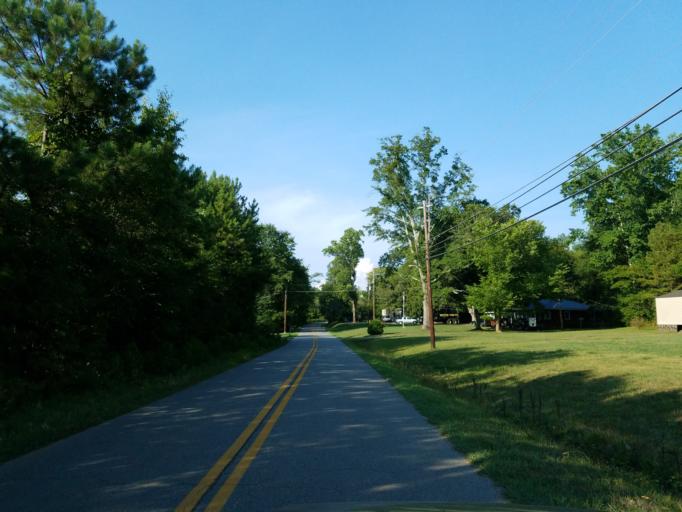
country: US
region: Georgia
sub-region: Bartow County
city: Rydal
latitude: 34.3437
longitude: -84.7314
